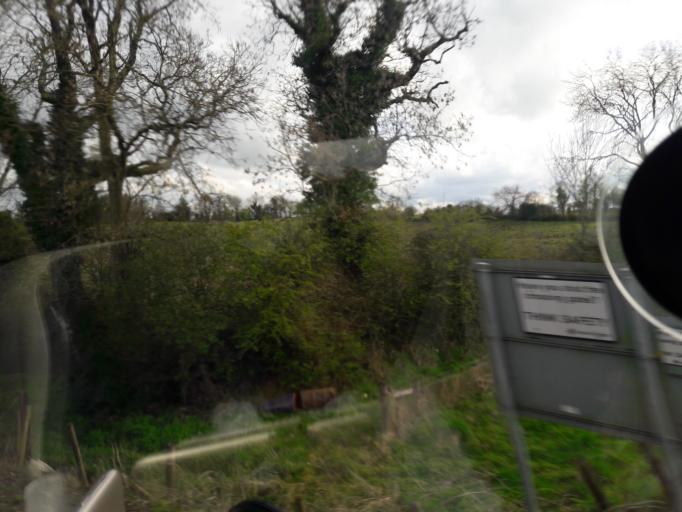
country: IE
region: Leinster
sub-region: An Iarmhi
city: An Muileann gCearr
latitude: 53.5035
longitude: -7.2753
